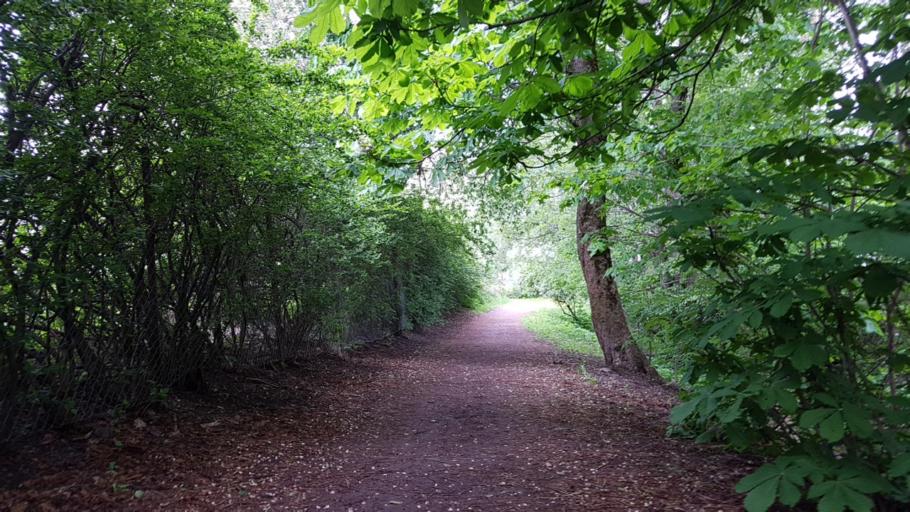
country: NO
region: Oslo
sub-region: Oslo
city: Oslo
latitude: 59.9422
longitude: 10.8213
